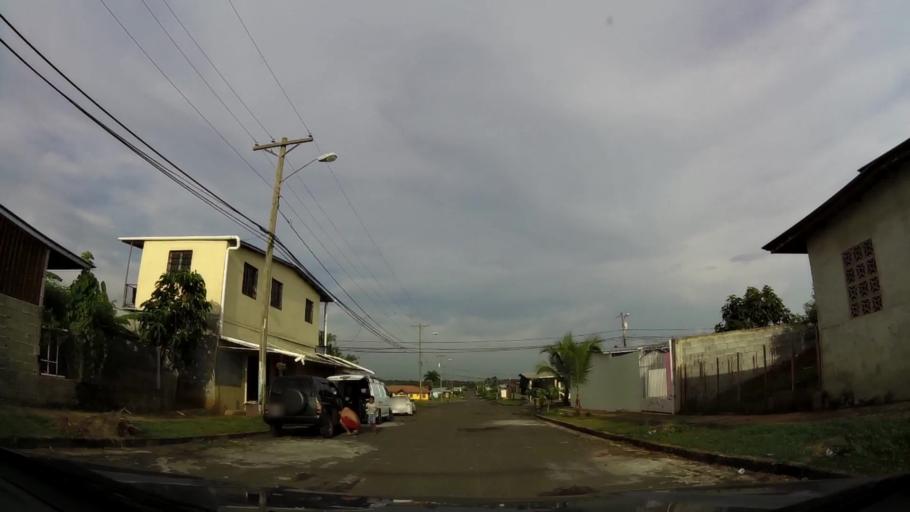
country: PA
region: Panama
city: Tocumen
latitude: 9.0775
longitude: -79.3578
